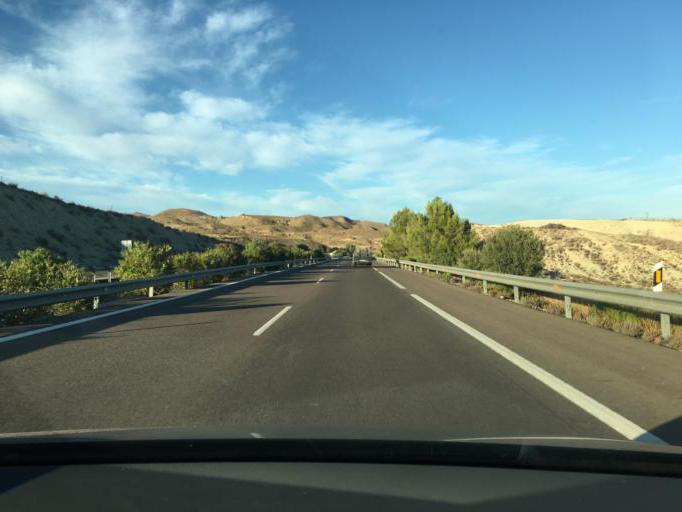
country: ES
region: Andalusia
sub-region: Provincia de Almeria
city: Bedar
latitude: 37.1318
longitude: -2.0099
